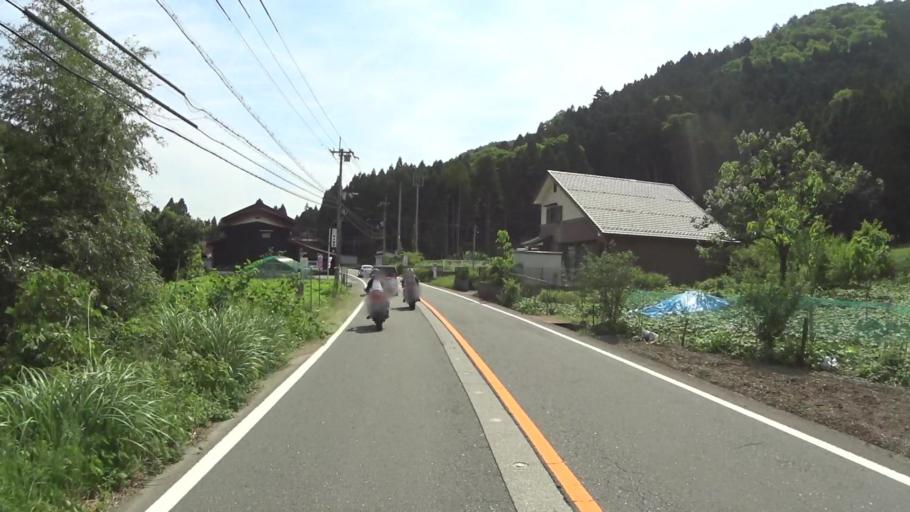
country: JP
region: Shiga Prefecture
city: Kitahama
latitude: 35.3347
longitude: 135.9024
